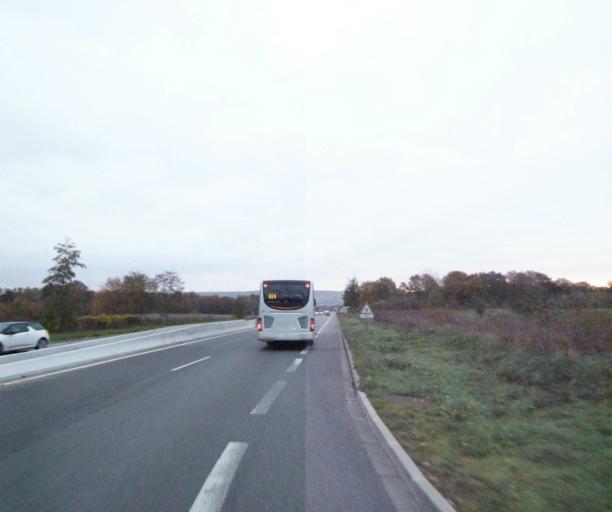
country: FR
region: Ile-de-France
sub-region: Departement des Yvelines
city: Vernouillet
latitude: 48.9589
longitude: 1.9804
